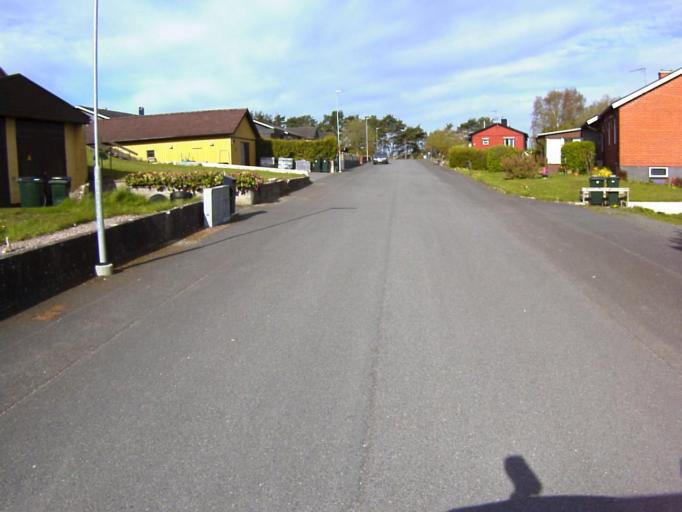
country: SE
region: Skane
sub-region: Kristianstads Kommun
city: Norra Asum
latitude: 55.9931
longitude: 14.1418
